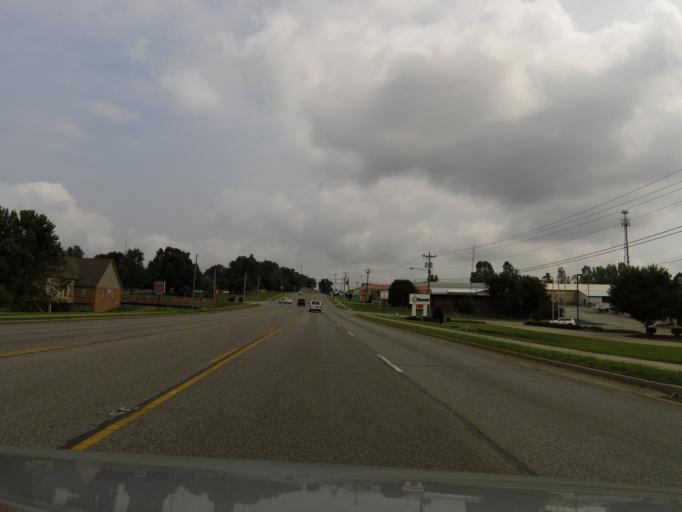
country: US
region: Kentucky
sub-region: Hopkins County
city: Madisonville
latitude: 37.3596
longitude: -87.4971
